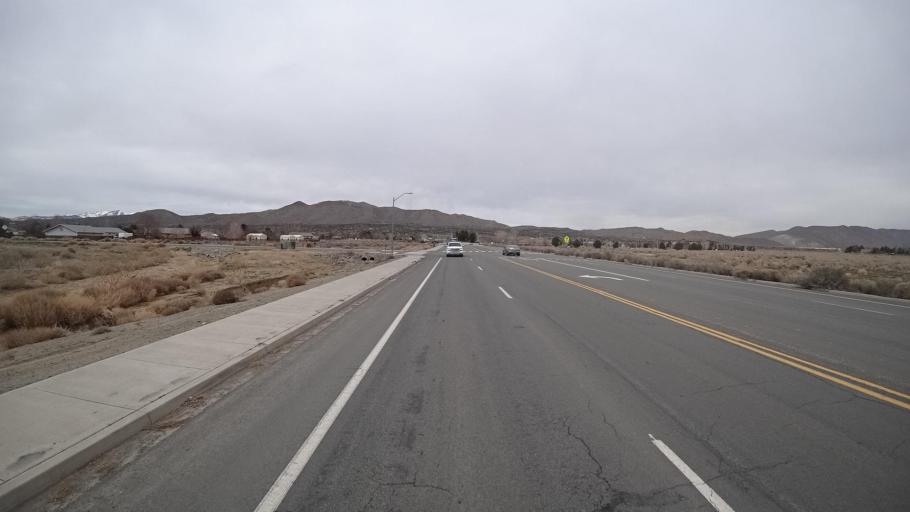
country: US
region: Nevada
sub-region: Washoe County
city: Spanish Springs
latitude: 39.6403
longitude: -119.7160
